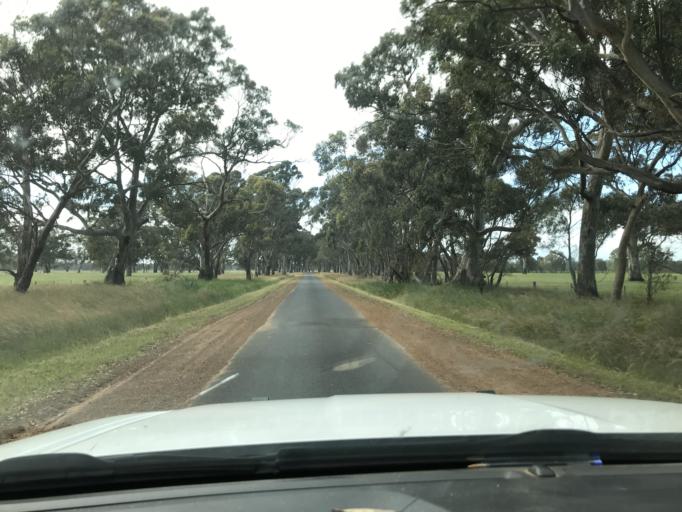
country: AU
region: South Australia
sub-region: Wattle Range
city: Penola
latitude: -37.1781
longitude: 141.2765
